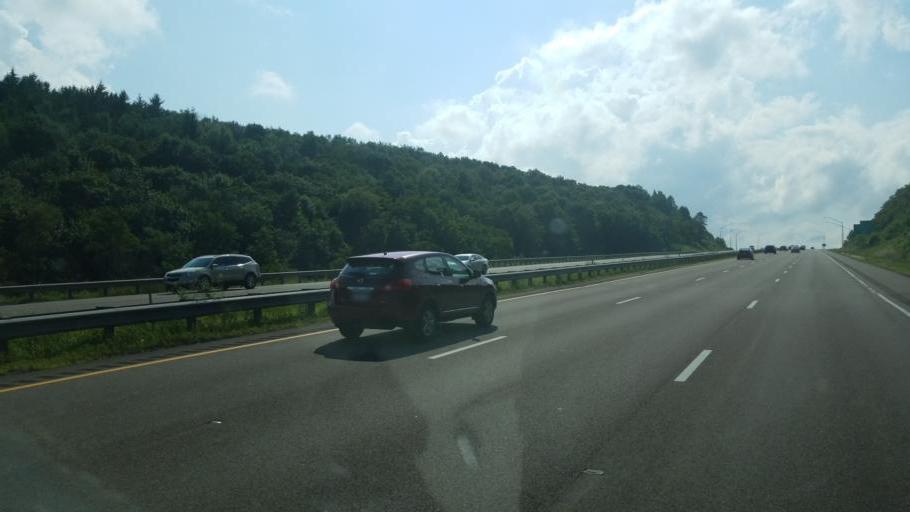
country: US
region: Pennsylvania
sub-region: Somerset County
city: Meyersdale
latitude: 39.6826
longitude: -79.0636
